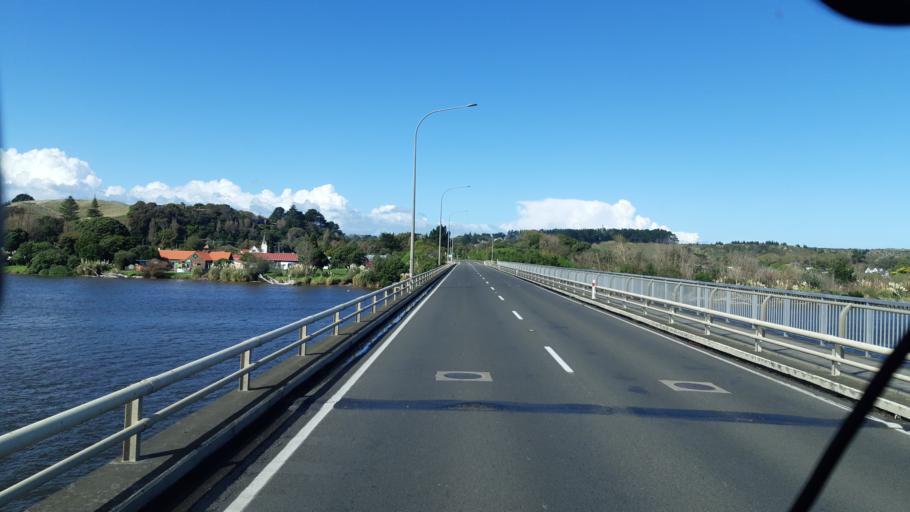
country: NZ
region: Manawatu-Wanganui
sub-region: Wanganui District
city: Wanganui
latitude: -39.9448
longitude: 175.0458
